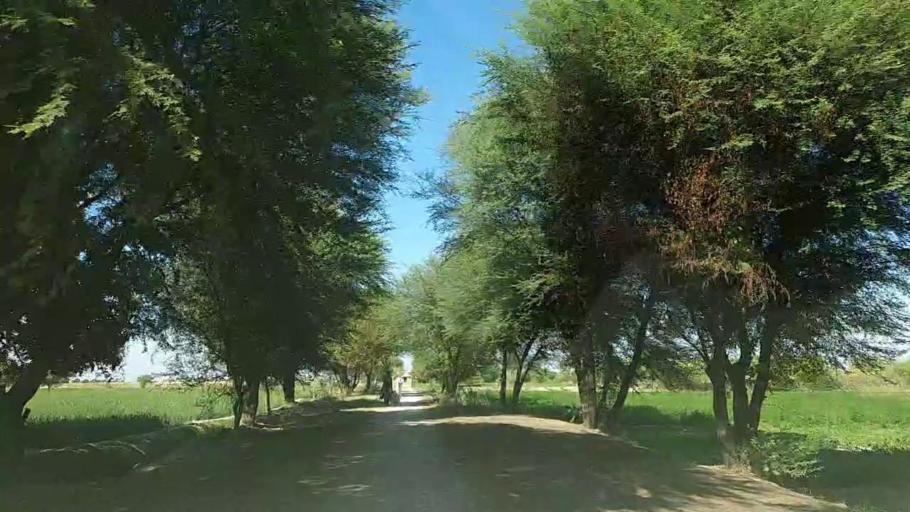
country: PK
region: Sindh
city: Samaro
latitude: 25.3046
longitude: 69.4649
